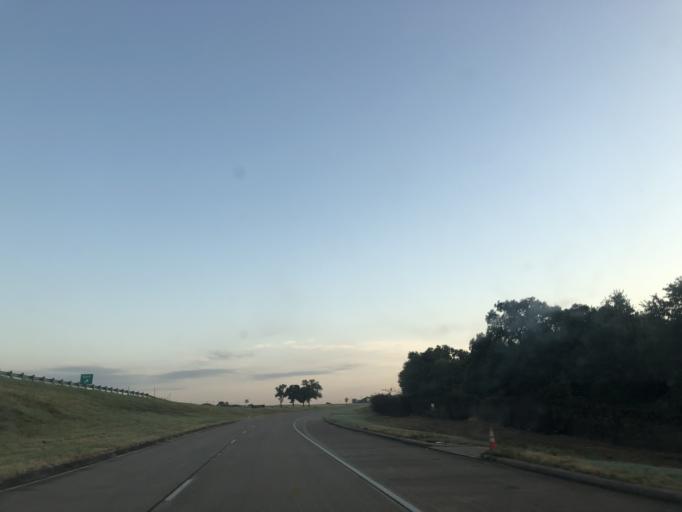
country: US
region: Texas
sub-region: Tarrant County
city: Euless
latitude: 32.8475
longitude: -97.0622
